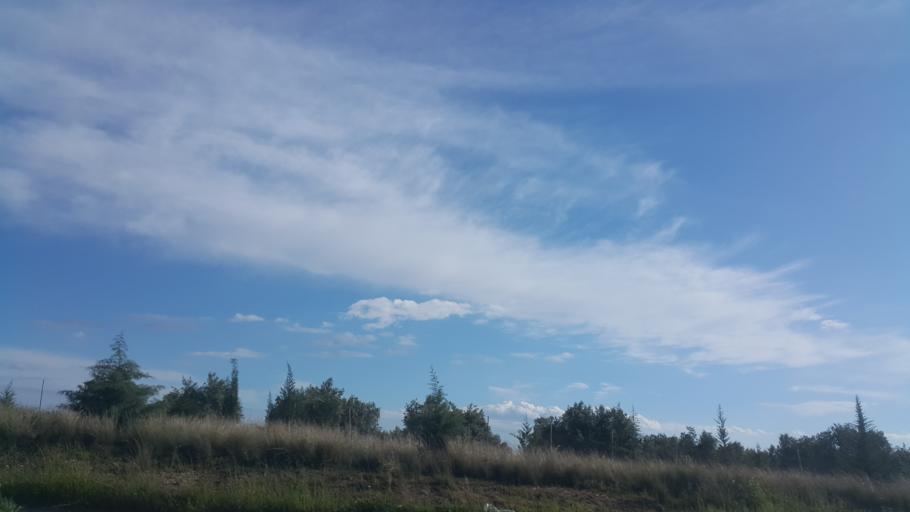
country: TR
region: Adana
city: Yuregir
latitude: 37.0204
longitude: 35.4882
